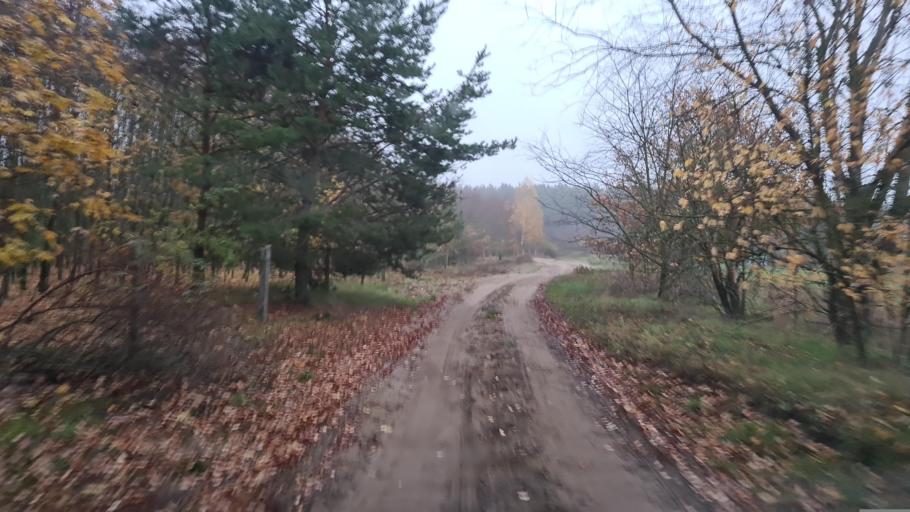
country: DE
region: Brandenburg
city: Beelitz
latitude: 52.2490
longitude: 13.0086
